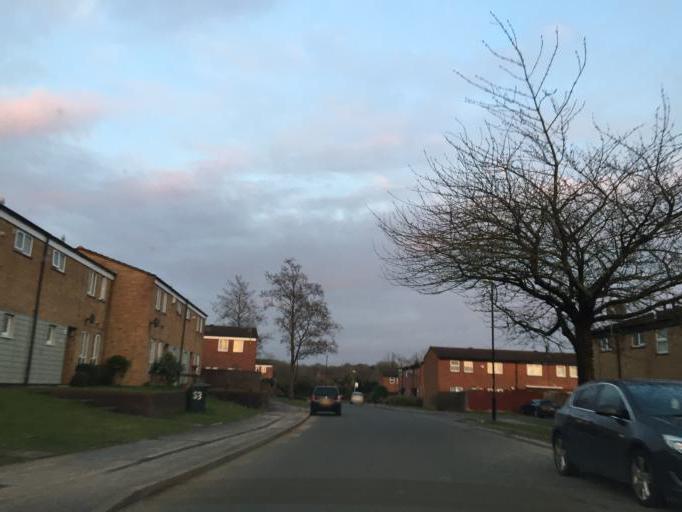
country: GB
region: England
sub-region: Solihull
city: Berkswell
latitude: 52.4026
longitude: -1.5974
